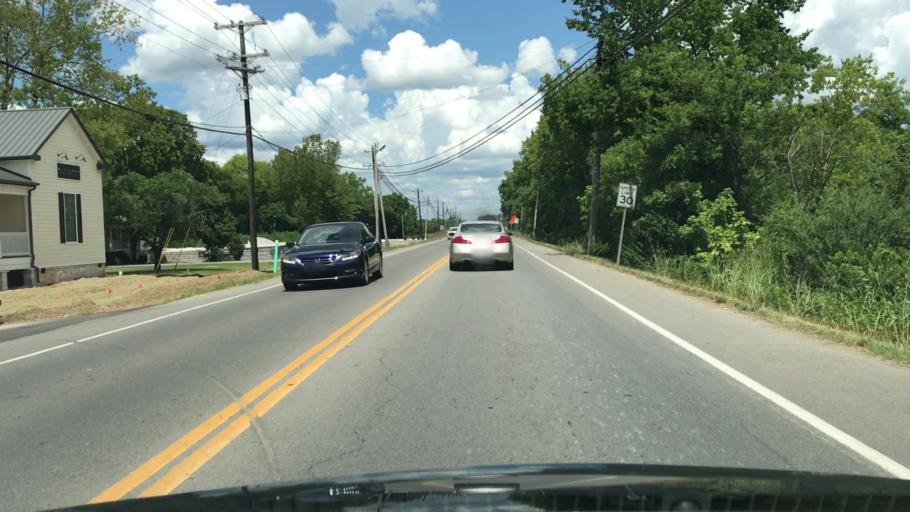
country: US
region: Tennessee
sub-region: Williamson County
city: Nolensville
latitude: 35.9548
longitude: -86.6708
